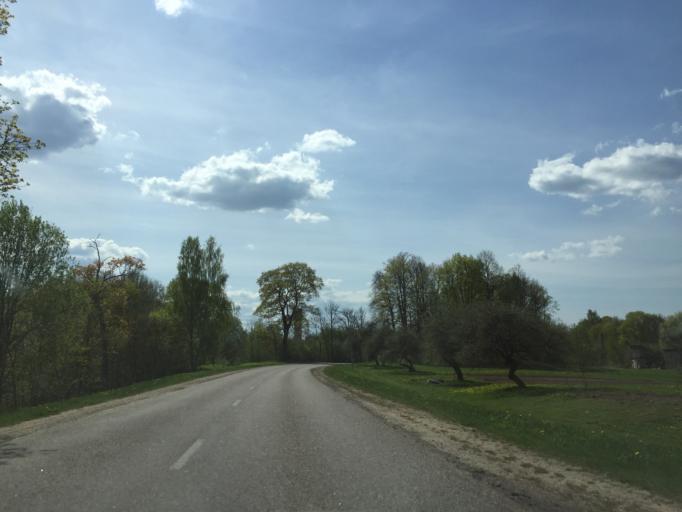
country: LV
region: Limbazu Rajons
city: Limbazi
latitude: 57.3492
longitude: 24.6639
